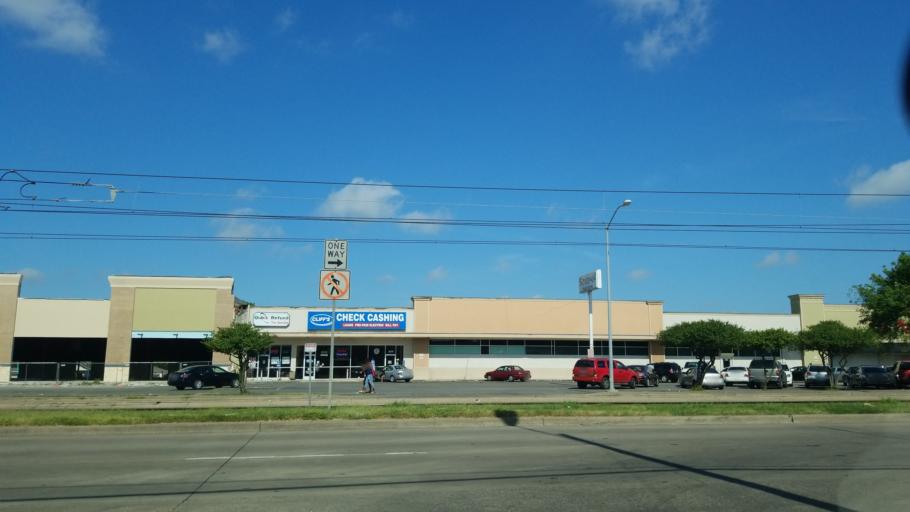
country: US
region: Texas
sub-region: Dallas County
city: Dallas
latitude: 32.7157
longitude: -96.8042
